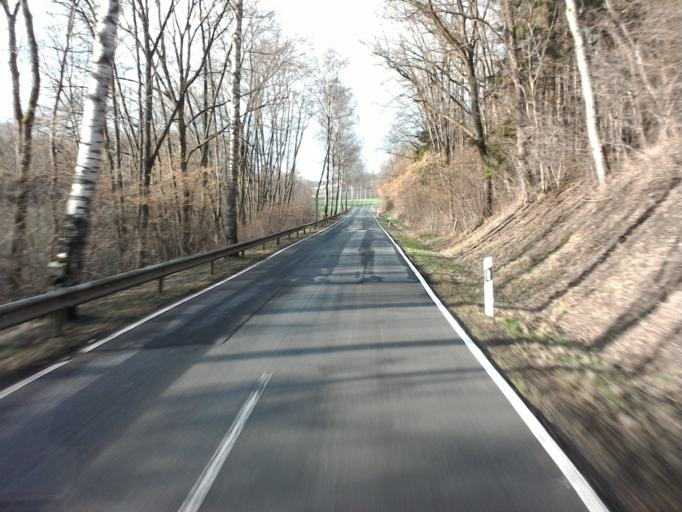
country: DE
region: Rheinland-Pfalz
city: Halsdorf
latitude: 49.9325
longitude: 6.3534
